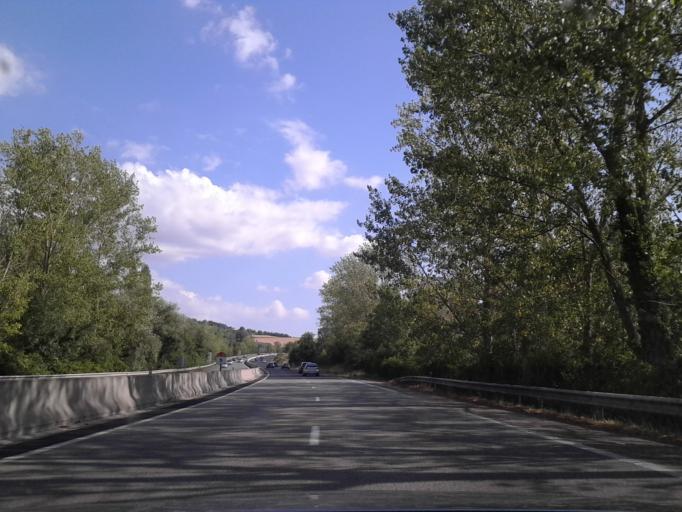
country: FR
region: Auvergne
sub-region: Departement du Puy-de-Dome
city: Orcet
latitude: 45.6966
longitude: 3.1481
